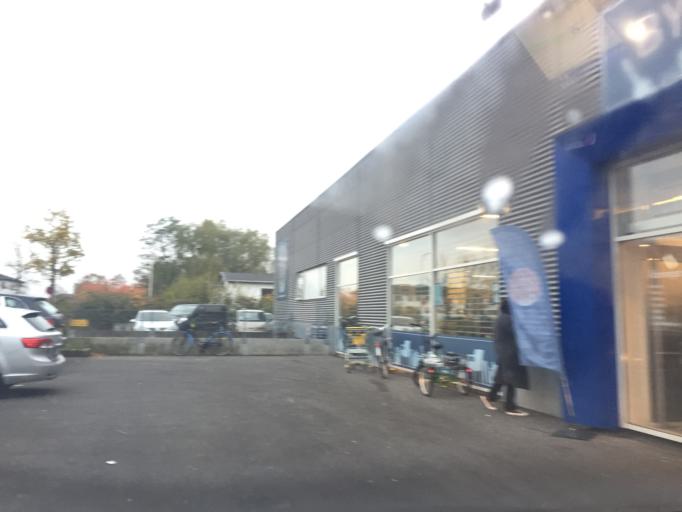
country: DK
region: Capital Region
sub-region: Gladsaxe Municipality
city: Buddinge
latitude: 55.7387
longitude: 12.4856
